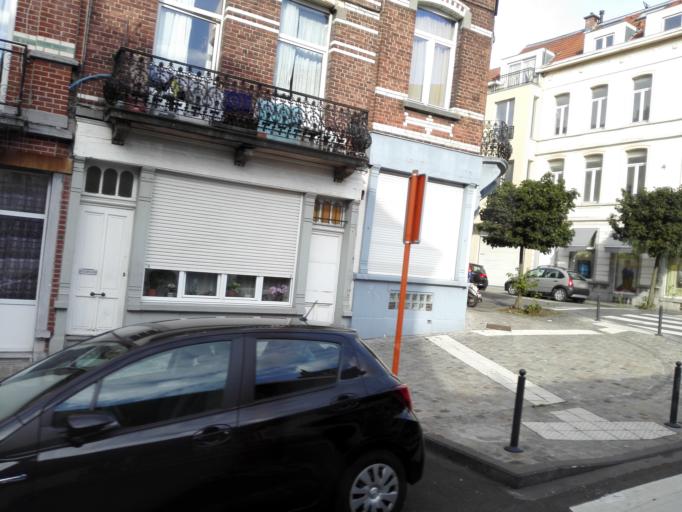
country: BE
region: Brussels Capital
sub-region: Bruxelles-Capitale
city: Brussels
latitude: 50.8539
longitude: 4.3860
